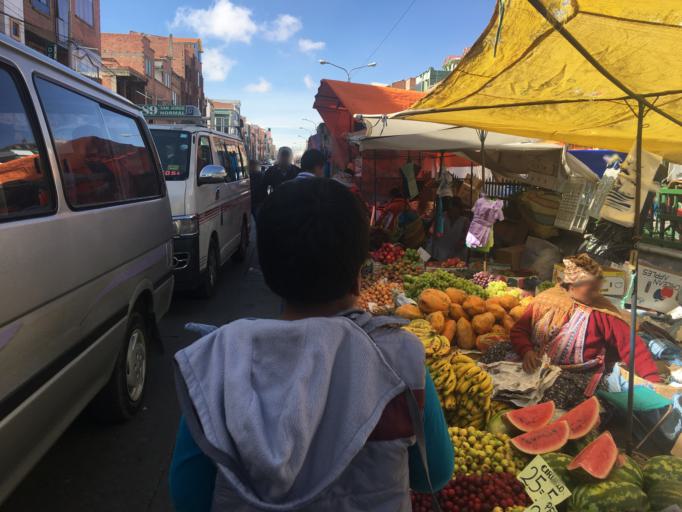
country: BO
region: La Paz
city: La Paz
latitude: -16.4892
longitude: -68.1719
